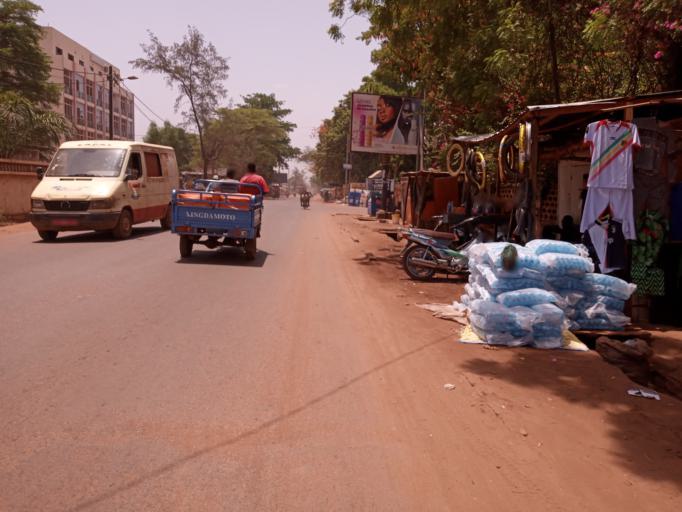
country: ML
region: Bamako
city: Bamako
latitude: 12.6488
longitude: -7.9748
